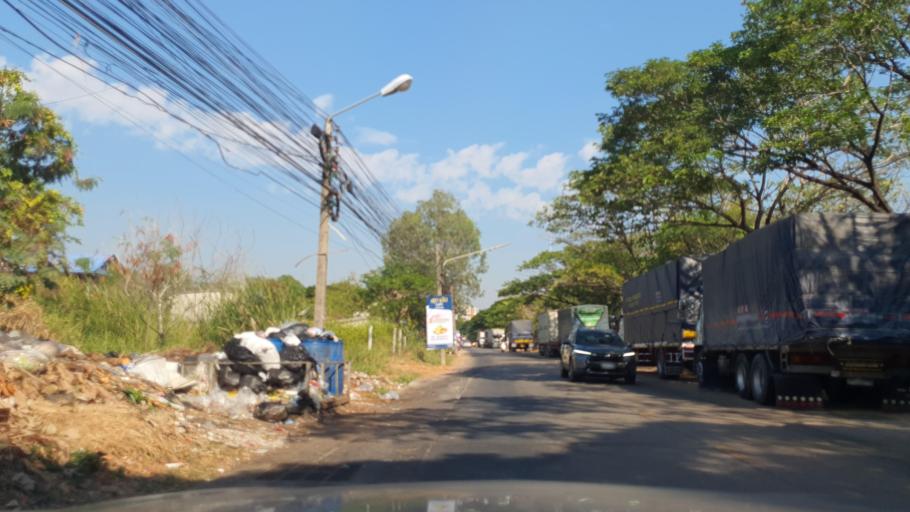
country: TH
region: Khon Kaen
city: Khon Kaen
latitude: 16.4352
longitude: 102.8145
